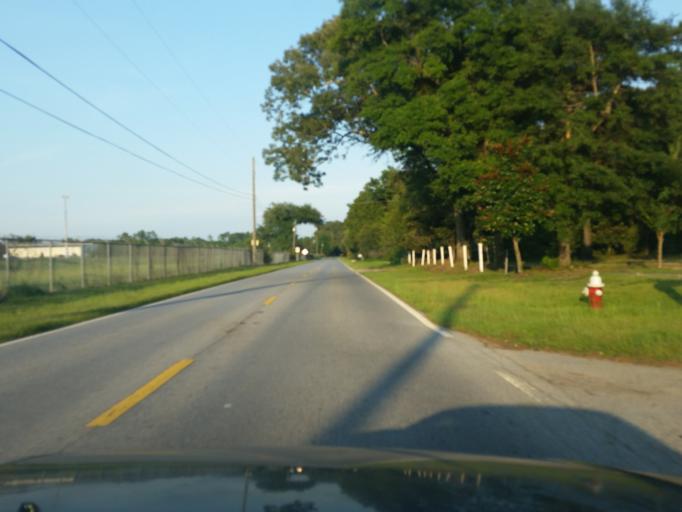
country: US
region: Florida
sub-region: Escambia County
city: Ferry Pass
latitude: 30.5172
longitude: -87.1977
